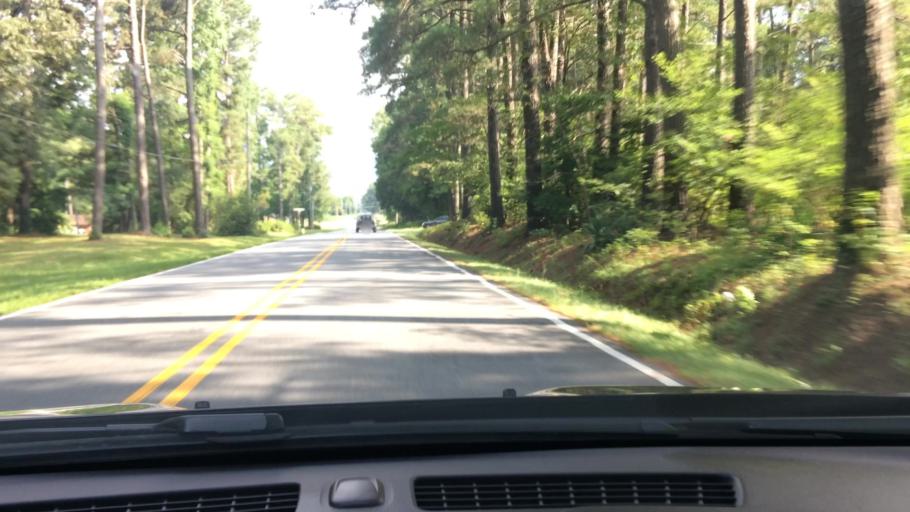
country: US
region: North Carolina
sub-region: Pitt County
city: Winterville
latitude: 35.5040
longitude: -77.3807
